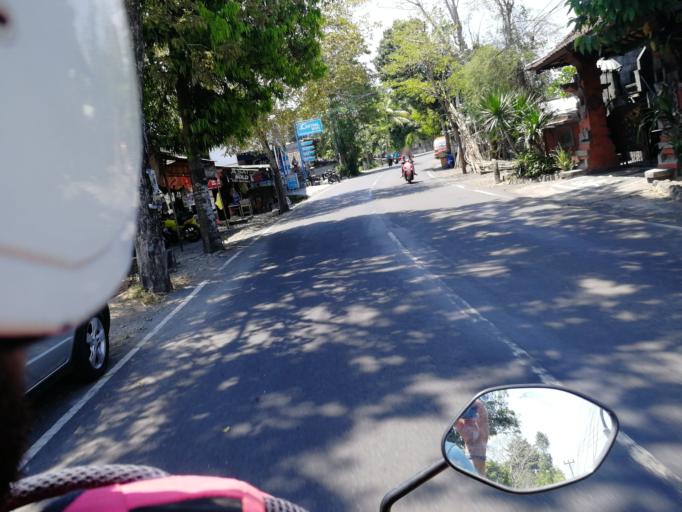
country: ID
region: Bali
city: Subagan
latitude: -8.4501
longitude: 115.5927
